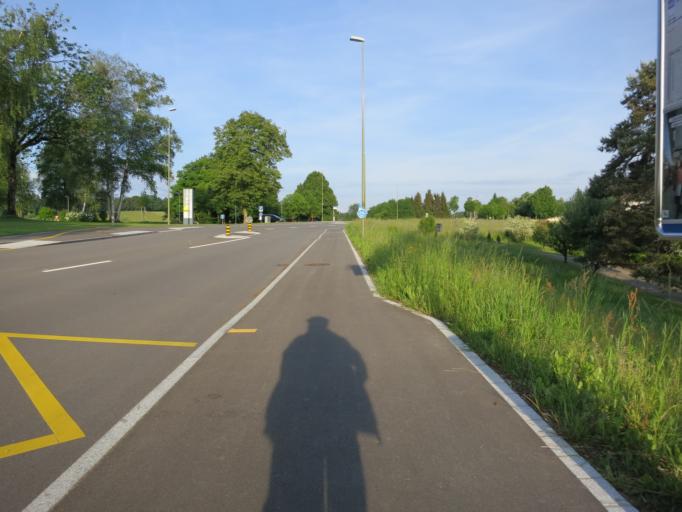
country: CH
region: Zurich
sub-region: Bezirk Hinwil
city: Gossau
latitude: 47.3000
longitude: 8.7669
